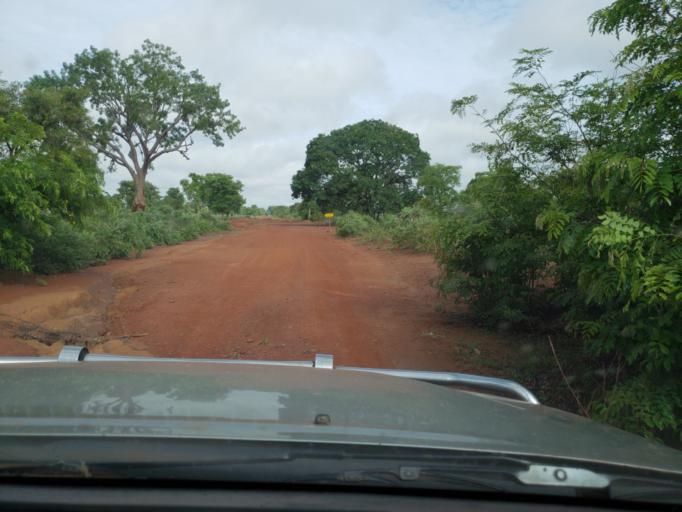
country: ML
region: Sikasso
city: Koutiala
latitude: 12.3925
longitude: -6.0052
